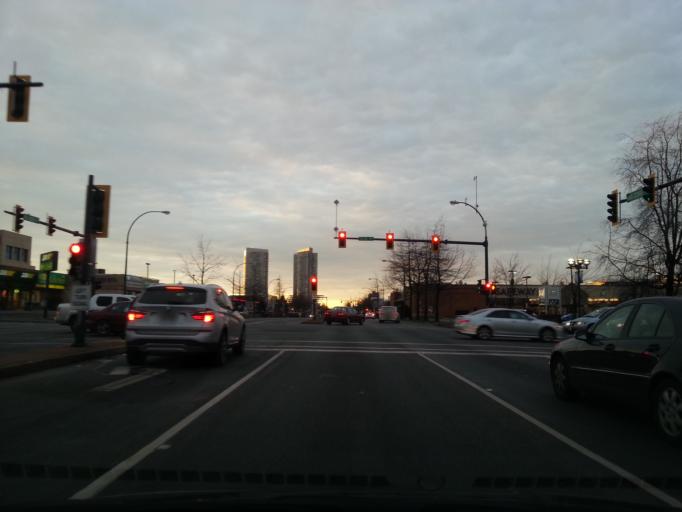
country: CA
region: British Columbia
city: New Westminster
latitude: 49.1919
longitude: -122.8455
